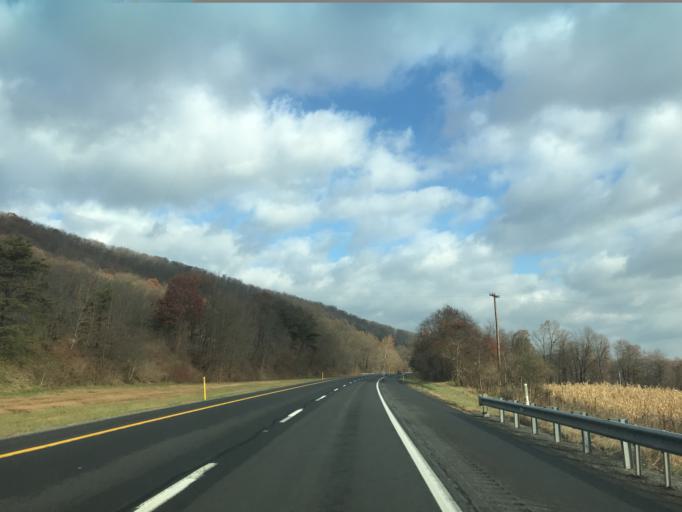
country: US
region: Maryland
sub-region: Washington County
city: Hancock
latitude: 39.8403
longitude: -78.2757
